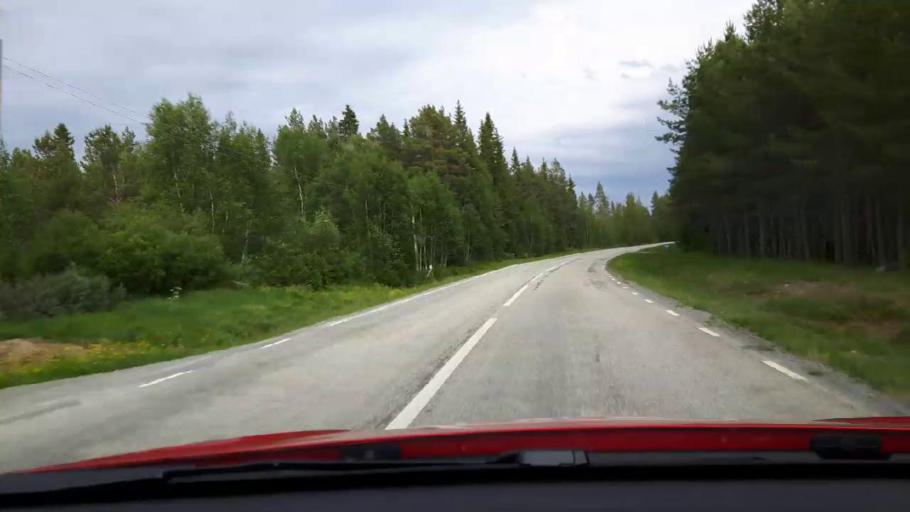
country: SE
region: Jaemtland
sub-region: Bergs Kommun
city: Hoverberg
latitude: 62.6630
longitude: 14.0508
